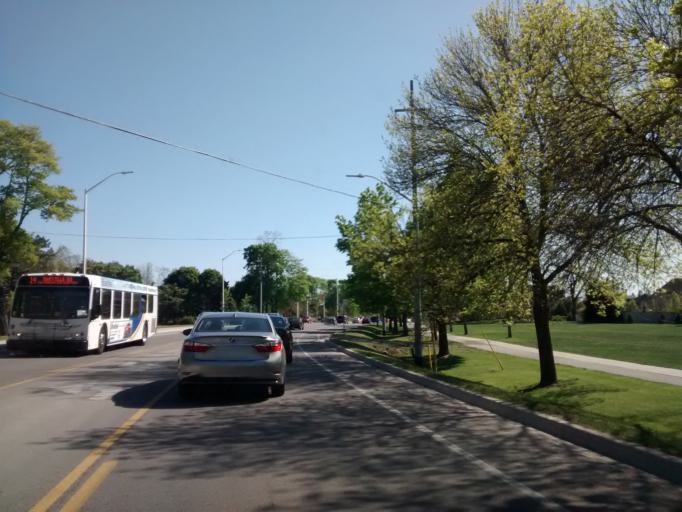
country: CA
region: Ontario
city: Oakville
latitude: 43.3777
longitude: -79.7177
